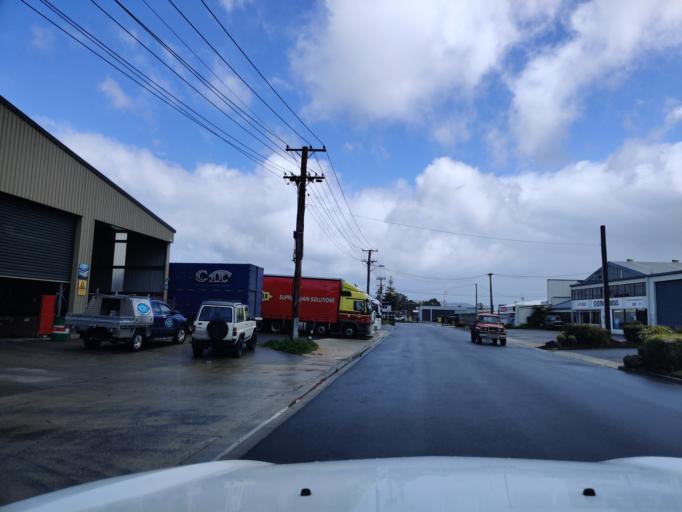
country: NZ
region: Bay of Plenty
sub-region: Rotorua District
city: Rotorua
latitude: -38.1456
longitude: 176.2776
